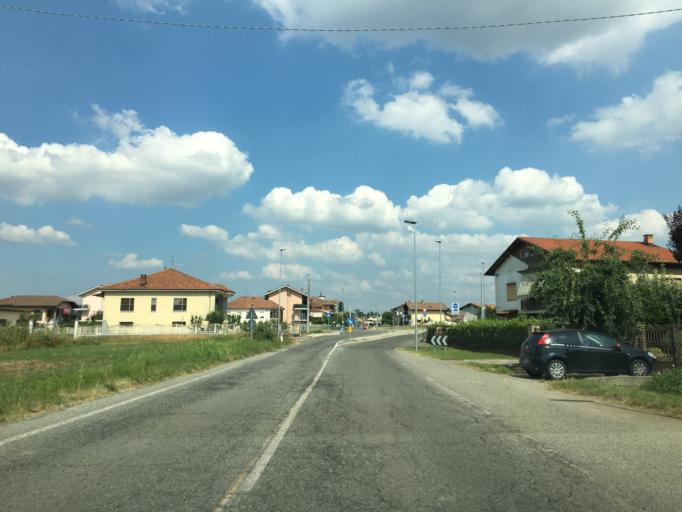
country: IT
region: Piedmont
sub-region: Provincia di Cuneo
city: Sommariva del Bosco
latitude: 44.7724
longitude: 7.7672
